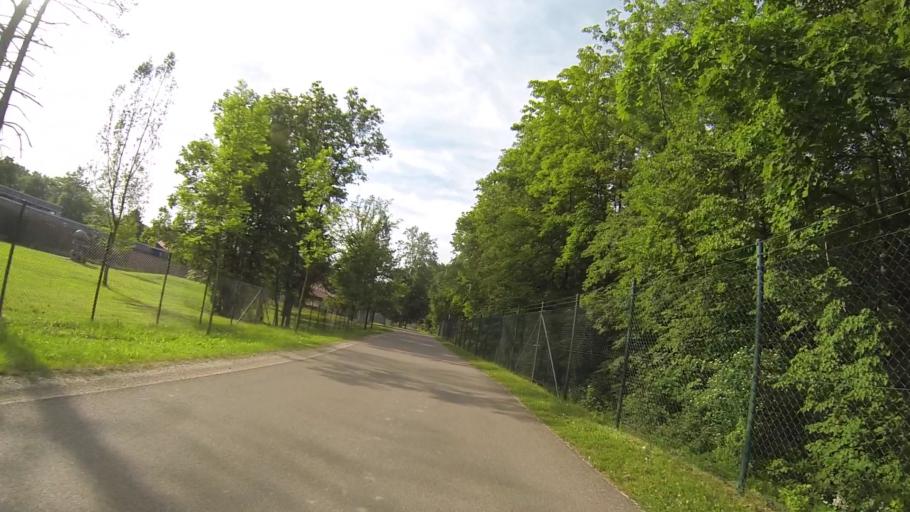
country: DE
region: Baden-Wuerttemberg
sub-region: Tuebingen Region
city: Ulm
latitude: 48.3734
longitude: 9.9661
